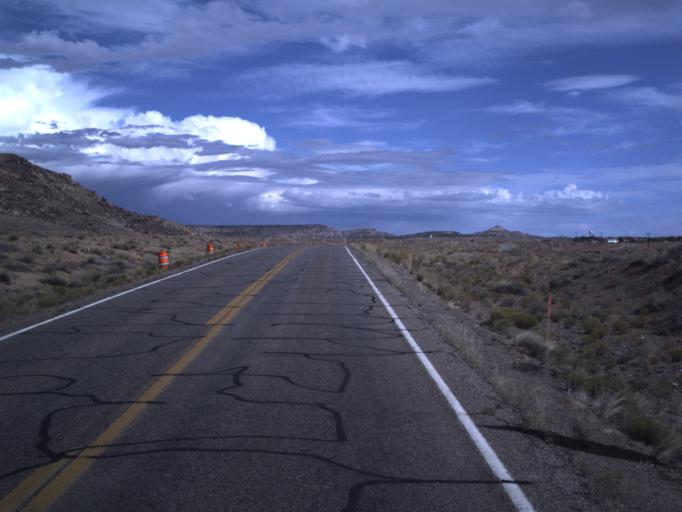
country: US
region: Colorado
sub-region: Montezuma County
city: Towaoc
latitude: 37.2136
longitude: -109.1782
